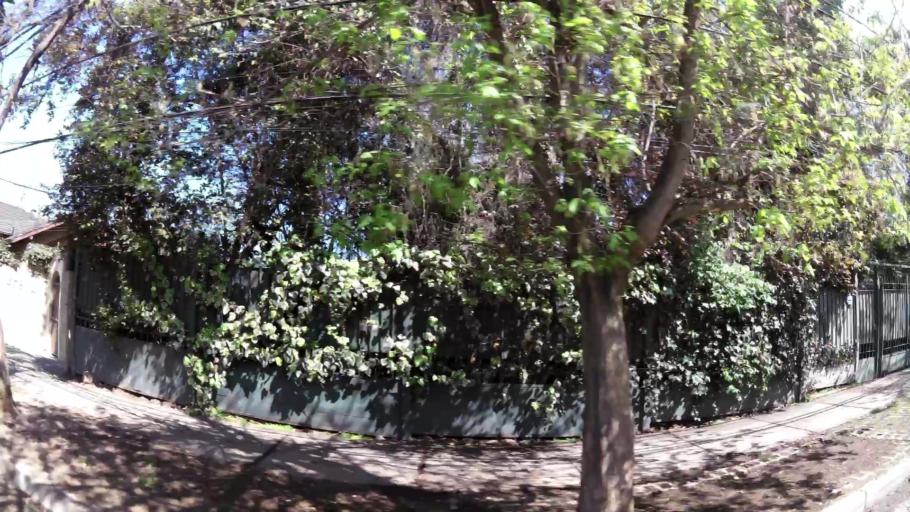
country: CL
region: Santiago Metropolitan
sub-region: Provincia de Santiago
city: Villa Presidente Frei, Nunoa, Santiago, Chile
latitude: -33.4495
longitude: -70.5240
